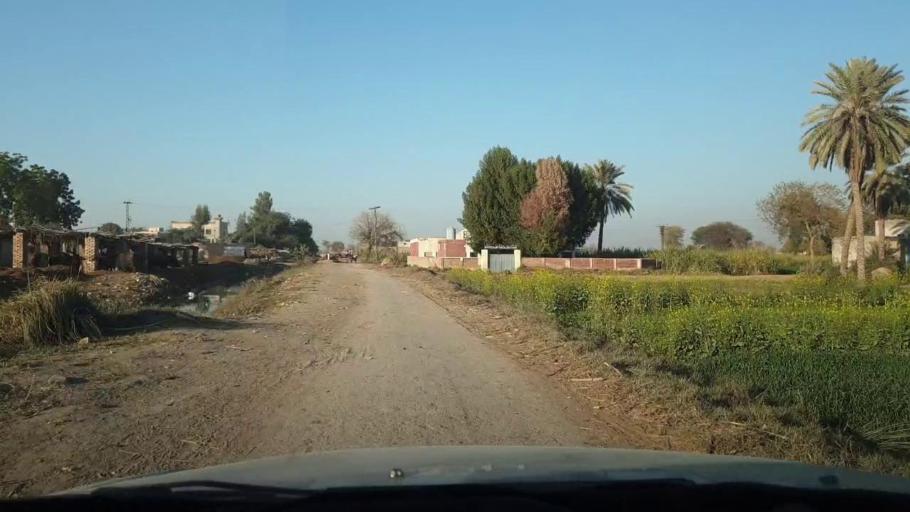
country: PK
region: Sindh
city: Ghotki
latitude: 27.9839
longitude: 69.2728
